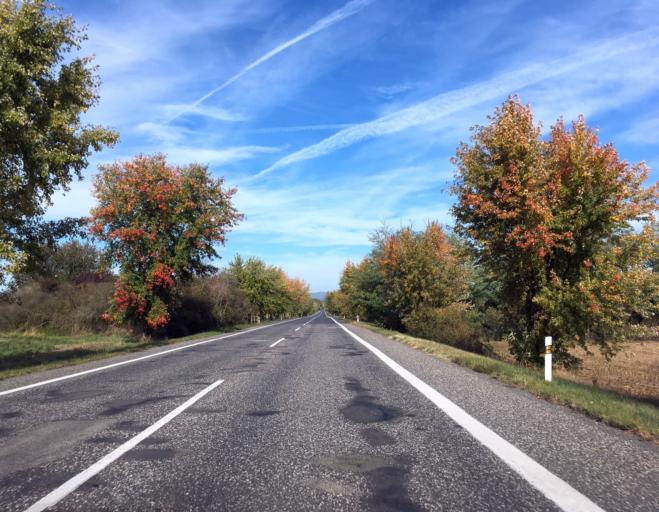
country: SK
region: Banskobystricky
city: Dudince
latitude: 48.1390
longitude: 18.8744
